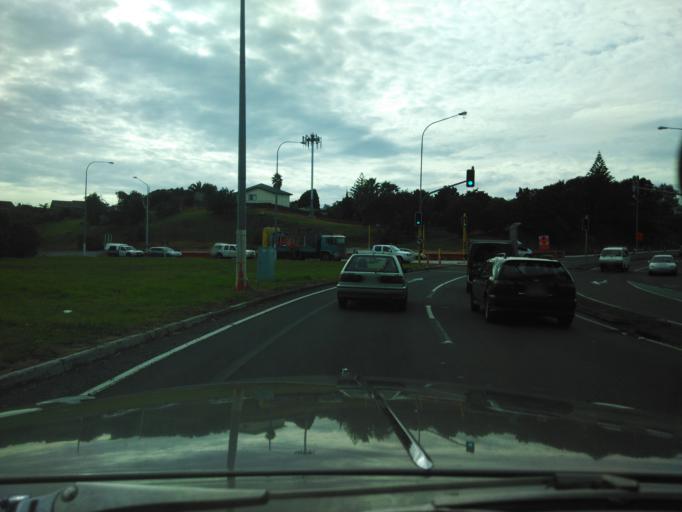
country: NZ
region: Auckland
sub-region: Auckland
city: Rosebank
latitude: -36.8720
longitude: 174.7050
